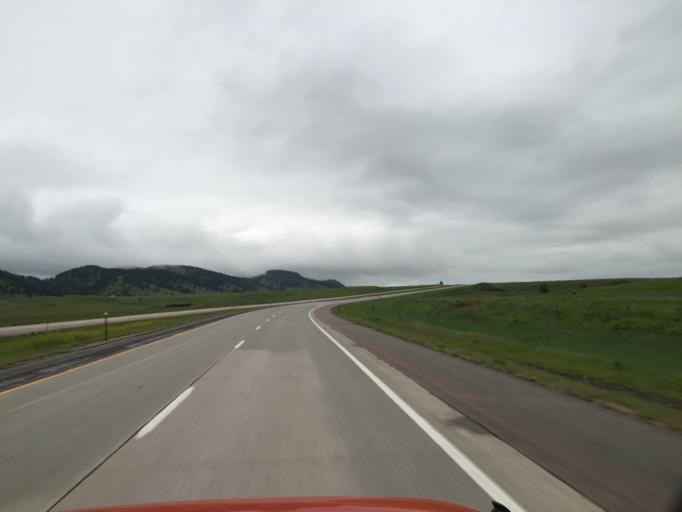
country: US
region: South Dakota
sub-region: Fall River County
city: Hot Springs
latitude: 43.4640
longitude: -103.3498
